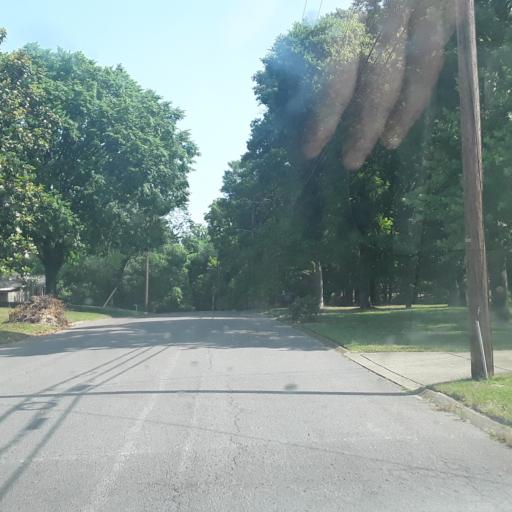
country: US
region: Tennessee
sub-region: Williamson County
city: Brentwood
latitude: 36.0498
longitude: -86.7473
